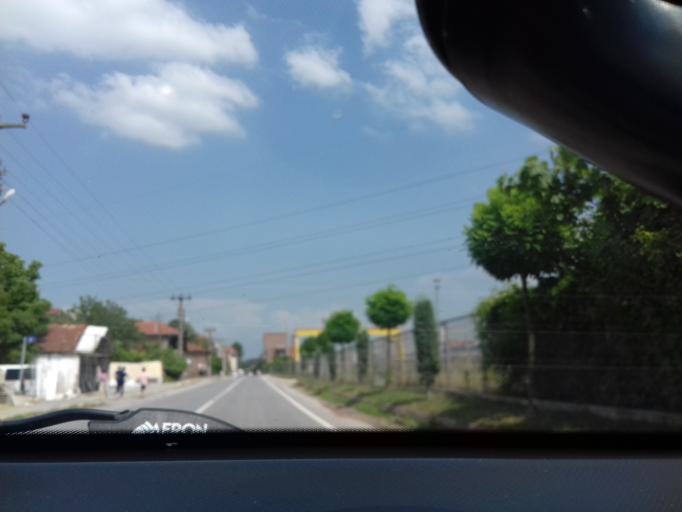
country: TR
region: Sakarya
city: Adapazari
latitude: 40.7136
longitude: 30.3517
